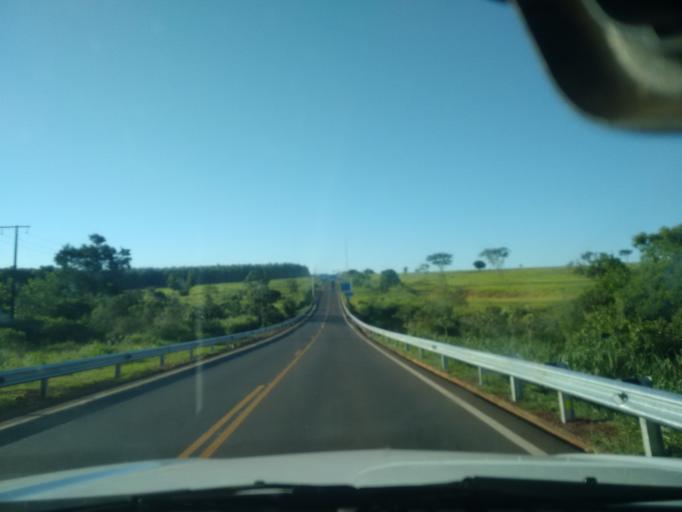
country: BR
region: Mato Grosso do Sul
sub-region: Eldorado
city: Eldorado
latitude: -23.8744
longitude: -54.3237
